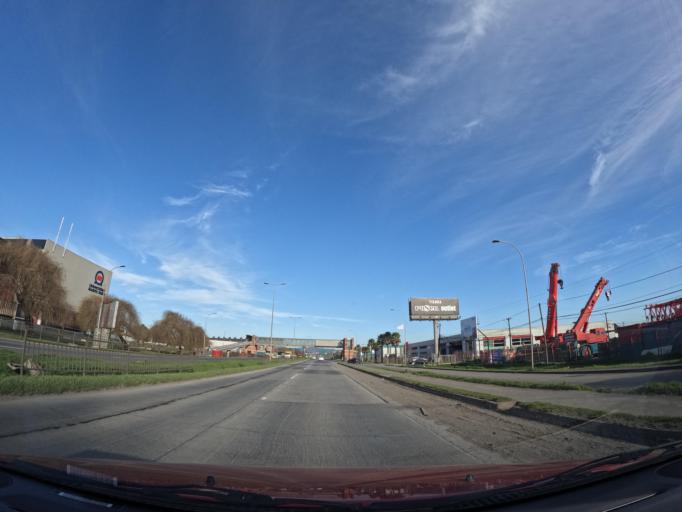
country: CL
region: Biobio
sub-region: Provincia de Concepcion
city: Concepcion
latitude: -36.7801
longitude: -73.0774
